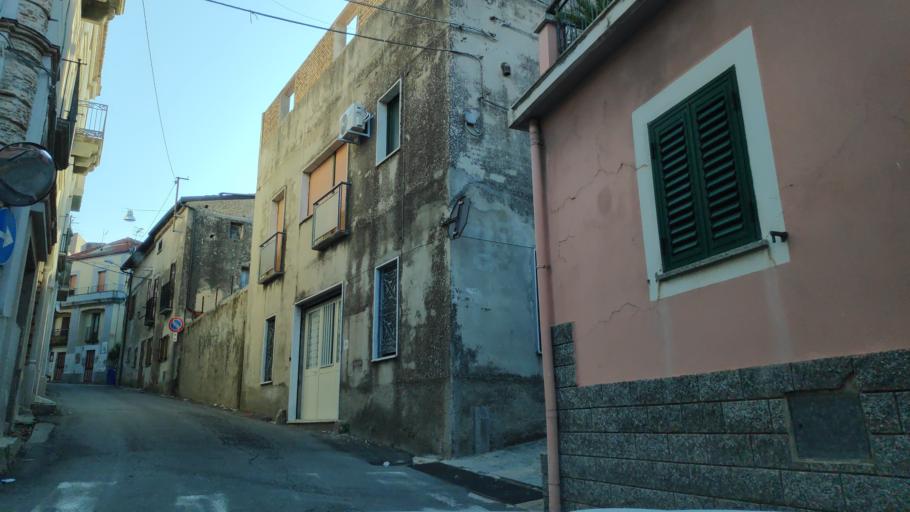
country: IT
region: Calabria
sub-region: Provincia di Catanzaro
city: Satriano
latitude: 38.6683
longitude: 16.4825
